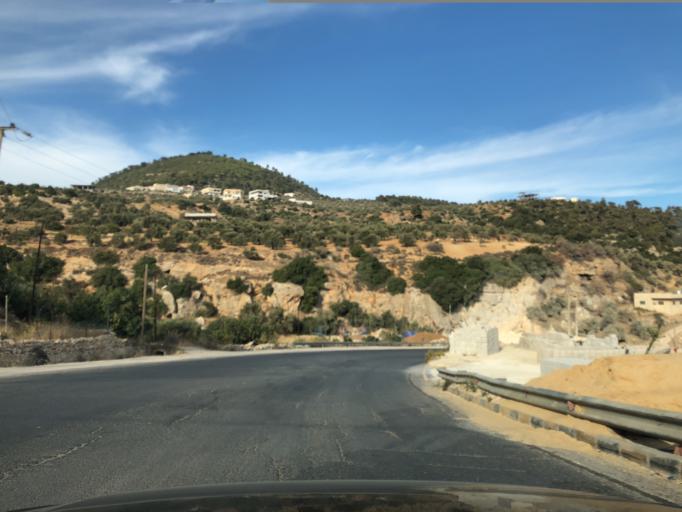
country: JO
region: Irbid
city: Sakib
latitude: 32.2848
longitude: 35.8138
